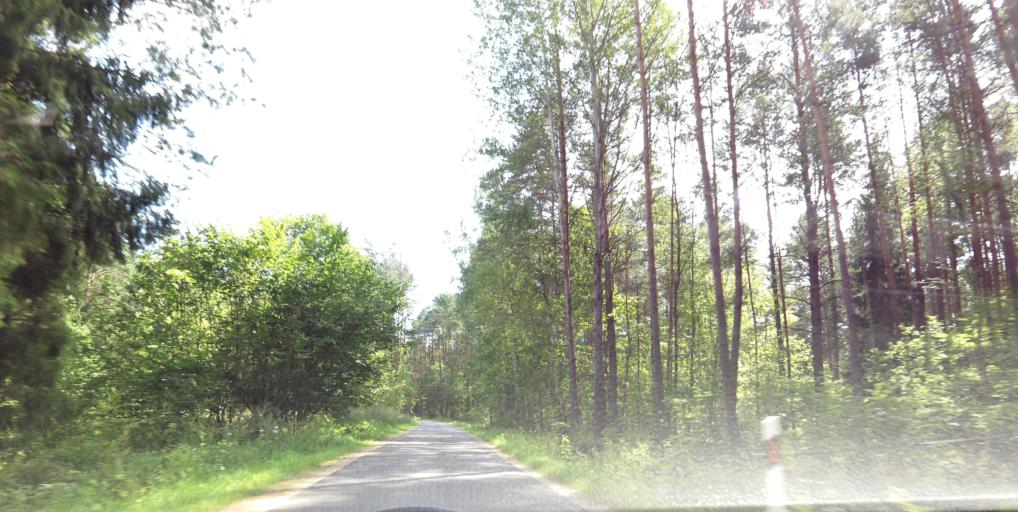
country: LT
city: Grigiskes
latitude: 54.7264
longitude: 25.0474
